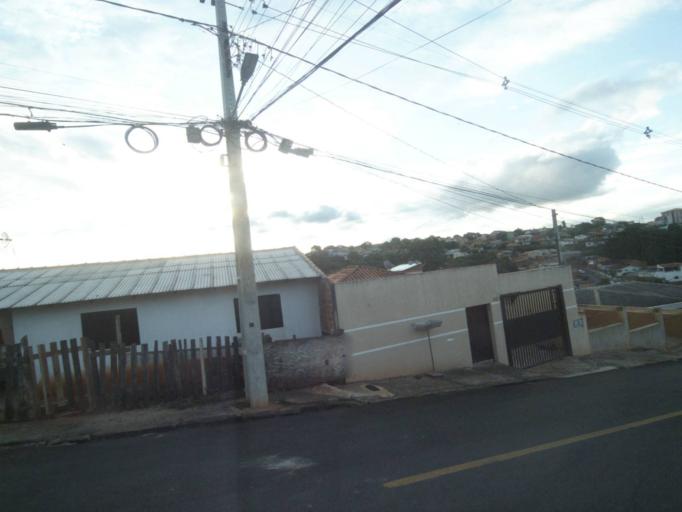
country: BR
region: Parana
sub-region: Telemaco Borba
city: Telemaco Borba
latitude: -24.3249
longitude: -50.6435
